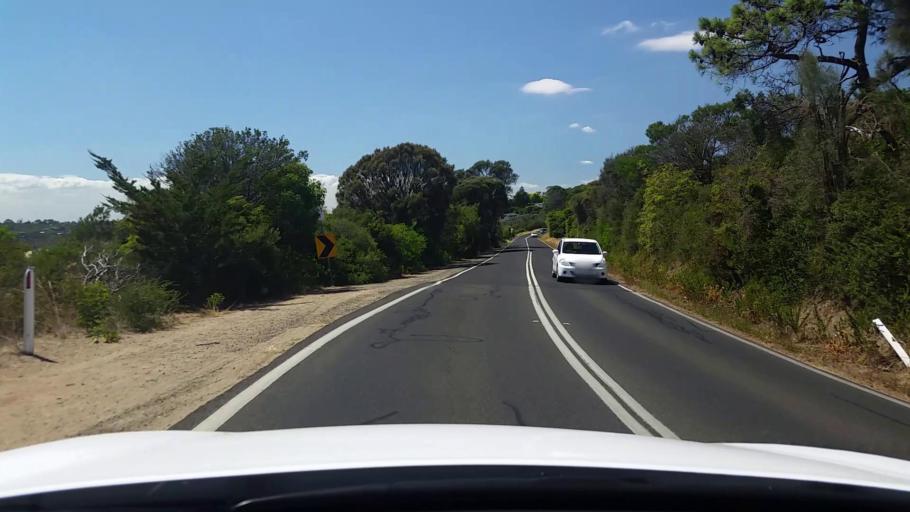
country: AU
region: Victoria
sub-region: Mornington Peninsula
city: Mount Martha
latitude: -38.2711
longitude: 145.0025
